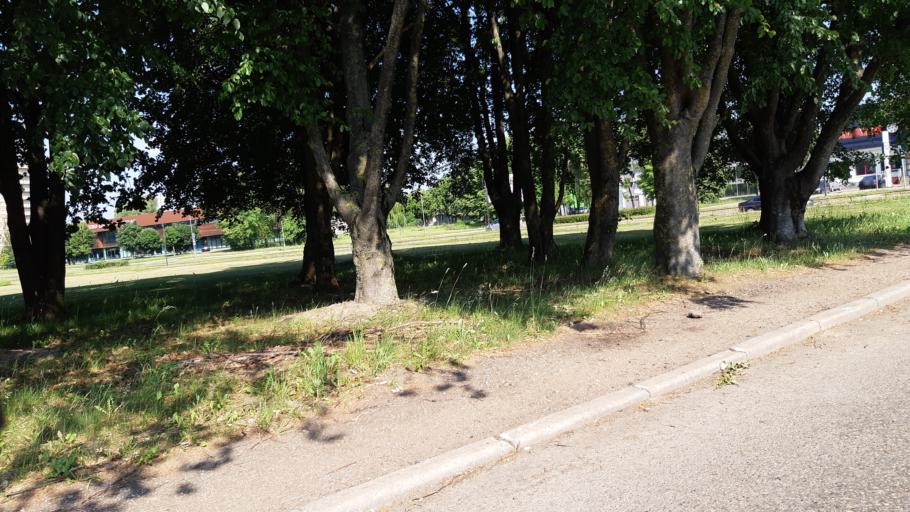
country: LT
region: Kauno apskritis
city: Dainava (Kaunas)
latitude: 54.9182
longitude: 23.9918
